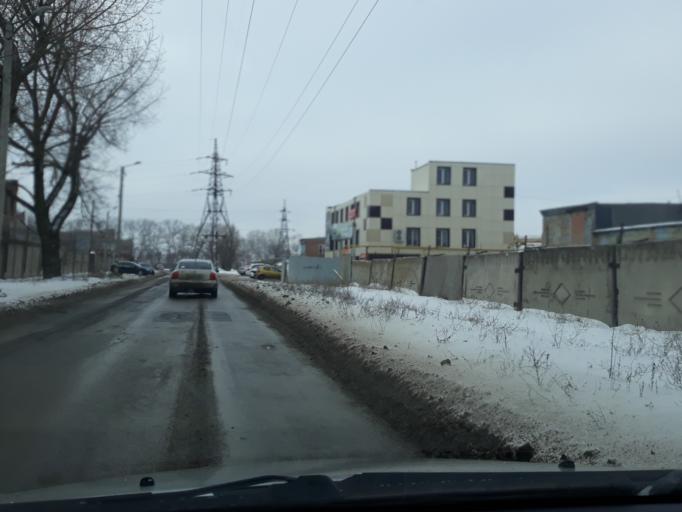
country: RU
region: Rostov
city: Taganrog
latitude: 47.2477
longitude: 38.8890
